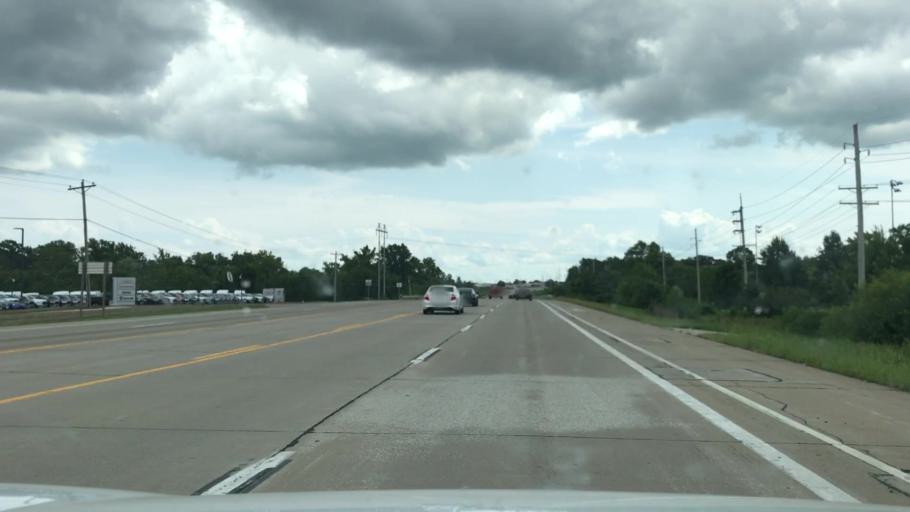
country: US
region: Missouri
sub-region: Saint Charles County
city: Weldon Spring
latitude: 38.7429
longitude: -90.6968
